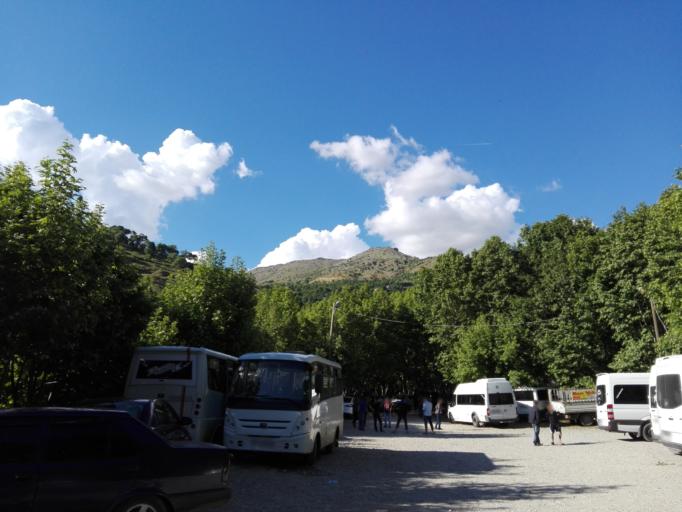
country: TR
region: Batman
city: Kozluk
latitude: 38.2160
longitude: 41.4828
